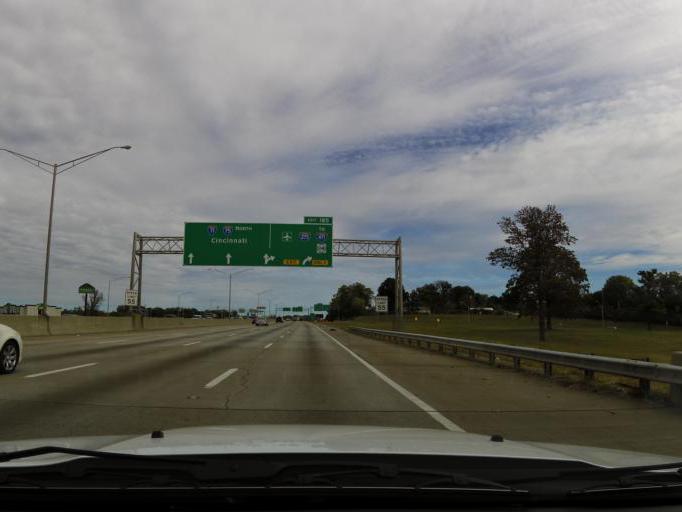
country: US
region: Kentucky
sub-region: Kenton County
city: Erlanger
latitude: 39.0258
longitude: -84.6126
